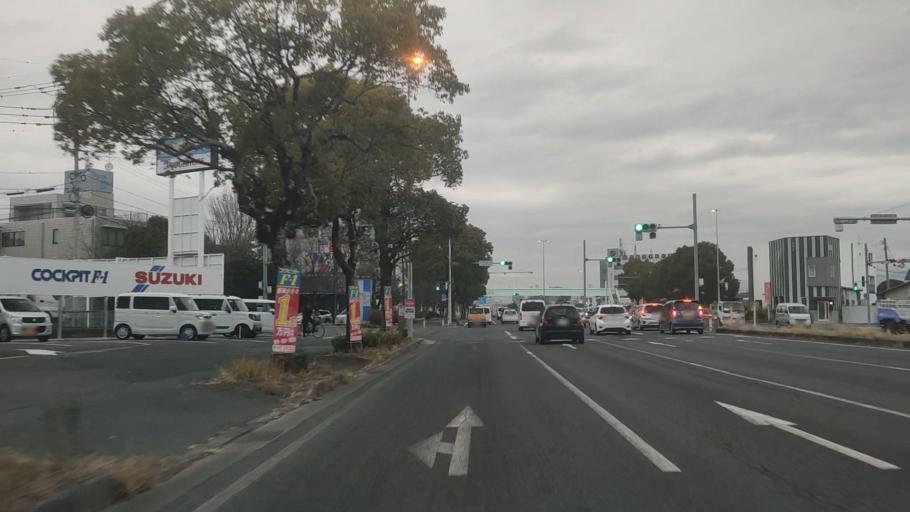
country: JP
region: Kumamoto
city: Kumamoto
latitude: 32.7737
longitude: 130.7343
